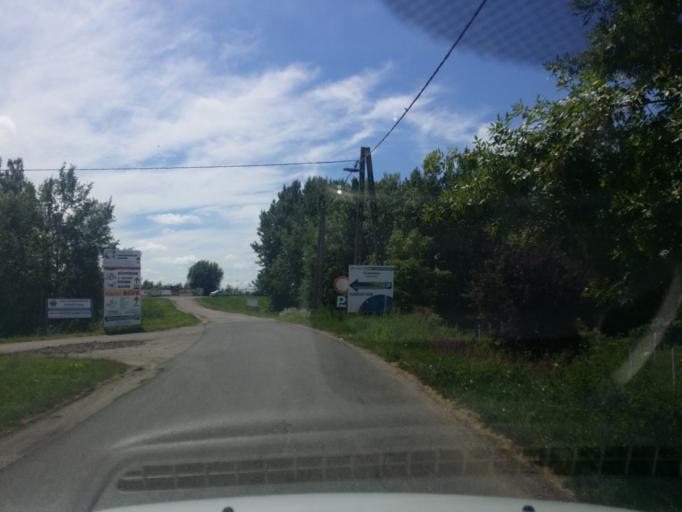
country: HU
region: Heves
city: Tiszanana
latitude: 47.5802
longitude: 20.6085
